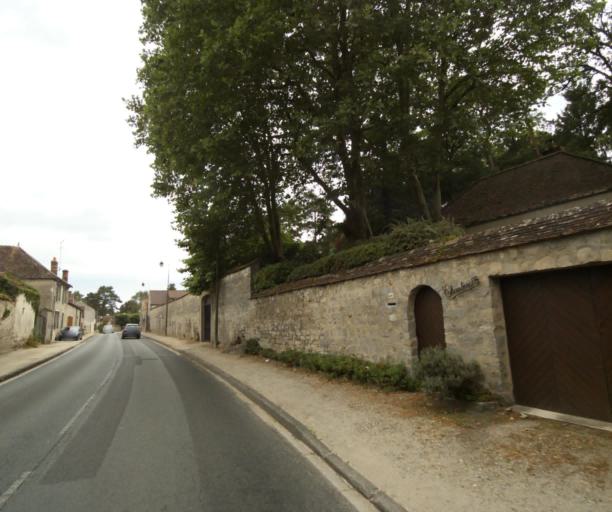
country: FR
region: Ile-de-France
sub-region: Departement de Seine-et-Marne
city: Arbonne-la-Foret
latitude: 48.4110
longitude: 2.5646
